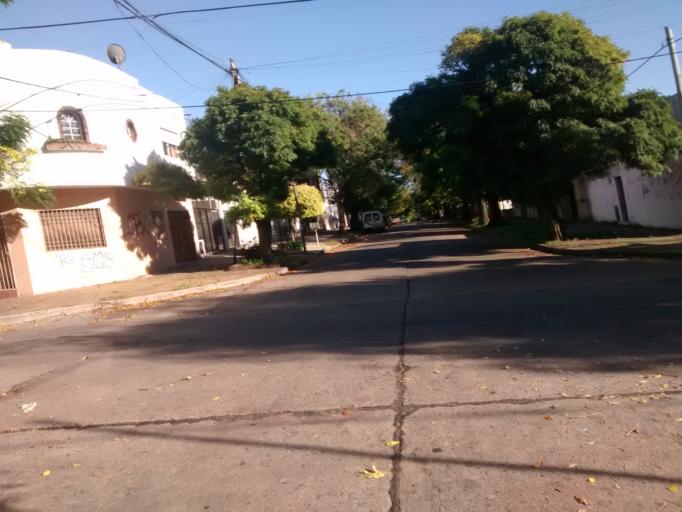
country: AR
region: Buenos Aires
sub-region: Partido de La Plata
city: La Plata
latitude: -34.9425
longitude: -57.9445
